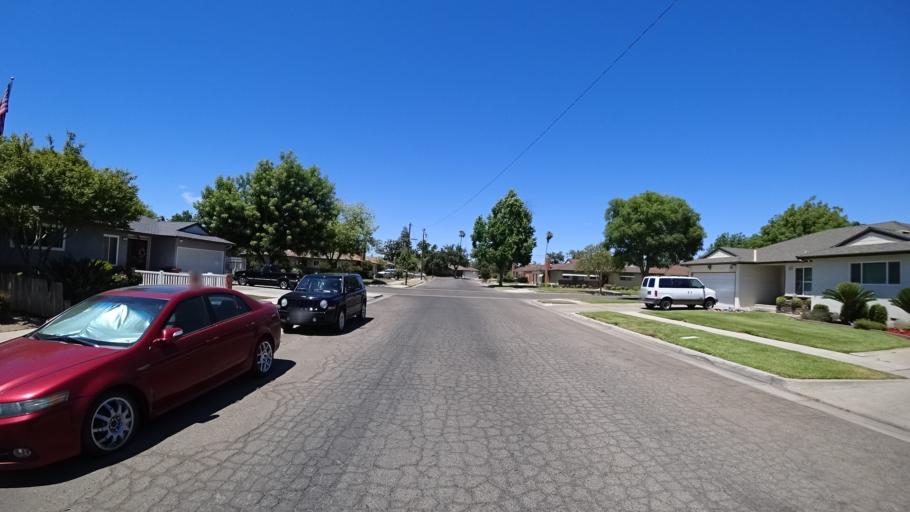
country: US
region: California
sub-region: Fresno County
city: Fresno
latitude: 36.8032
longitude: -119.7687
